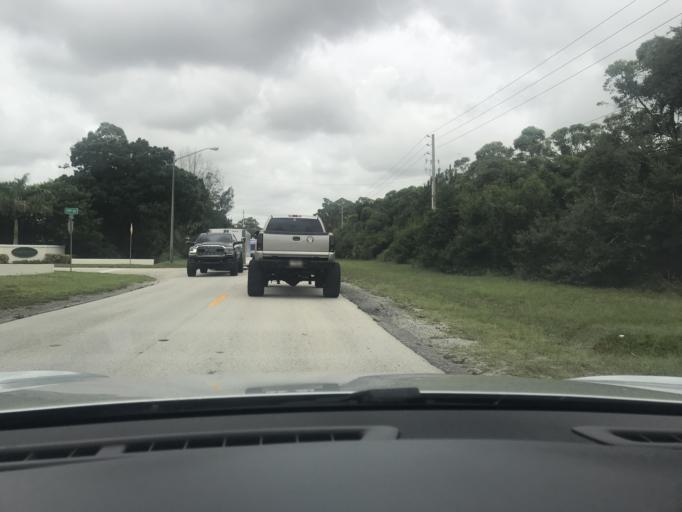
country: US
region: Florida
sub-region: Indian River County
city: Vero Beach South
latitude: 27.6461
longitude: -80.4434
